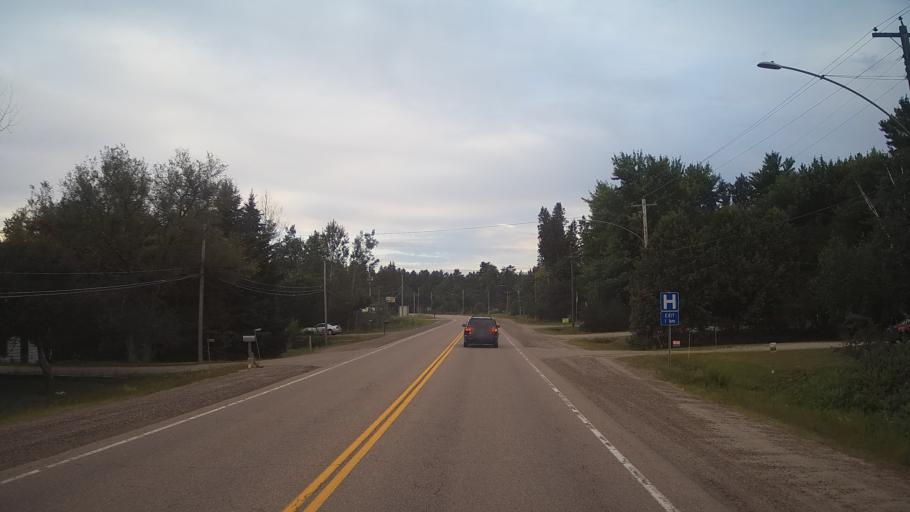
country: CA
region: Ontario
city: Deep River
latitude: 46.0909
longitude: -77.4907
